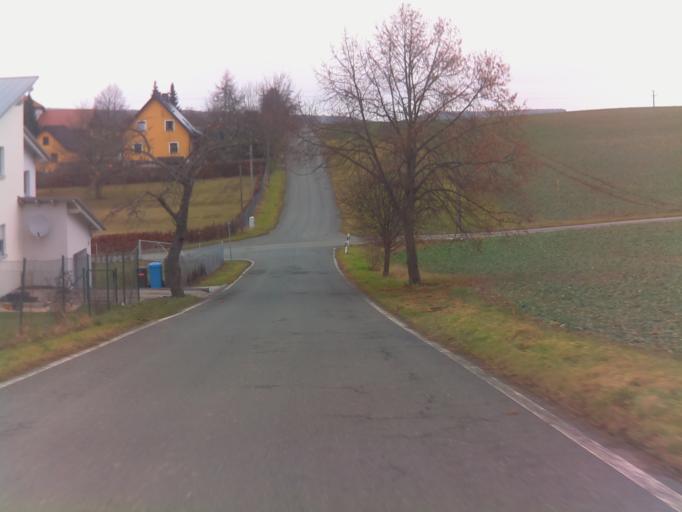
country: DE
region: Thuringia
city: Dreitzsch
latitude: 50.7276
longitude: 11.7890
